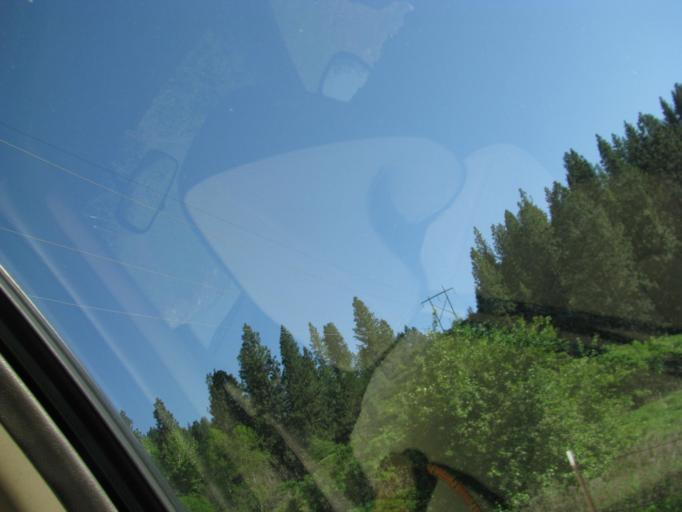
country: US
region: Washington
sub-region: Spokane County
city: Liberty Lake
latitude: 47.6111
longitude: -117.1079
